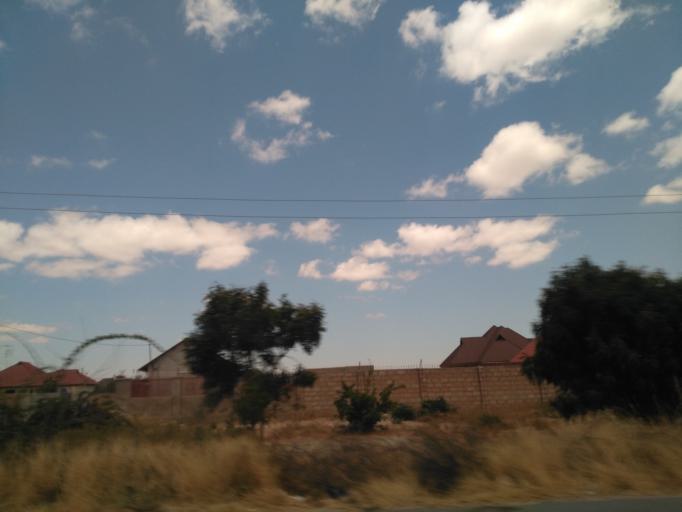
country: TZ
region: Dodoma
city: Kisasa
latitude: -6.1799
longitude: 35.7917
